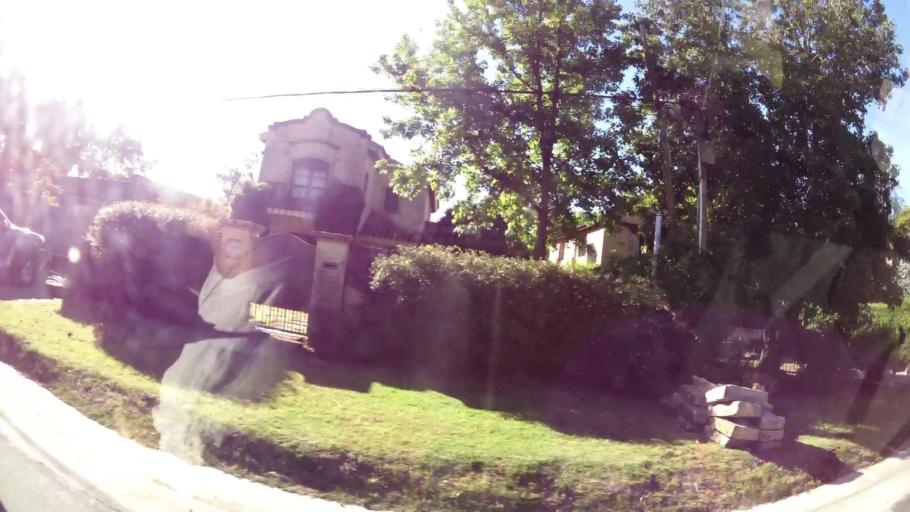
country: UY
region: Canelones
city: Barra de Carrasco
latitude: -34.8604
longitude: -56.0314
